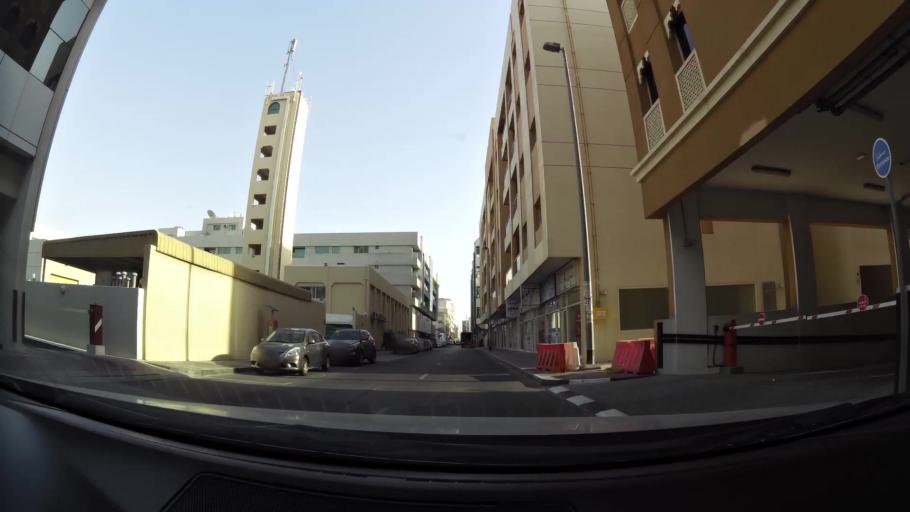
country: AE
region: Ash Shariqah
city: Sharjah
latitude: 25.2478
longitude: 55.3076
